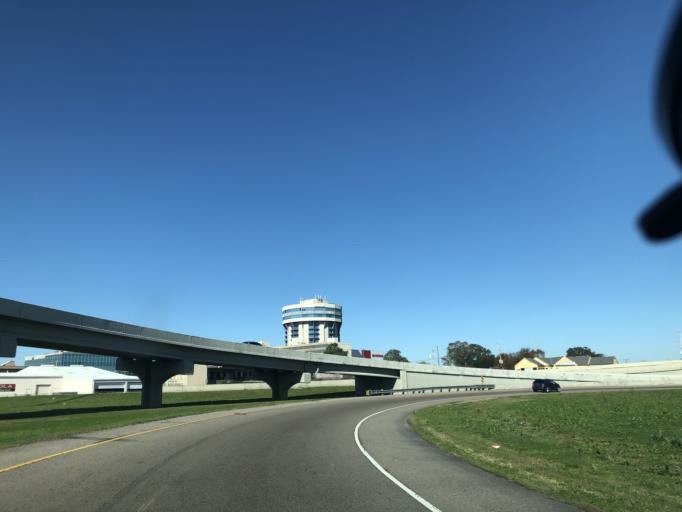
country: US
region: Louisiana
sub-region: Jefferson Parish
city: Metairie
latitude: 29.9979
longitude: -90.1566
